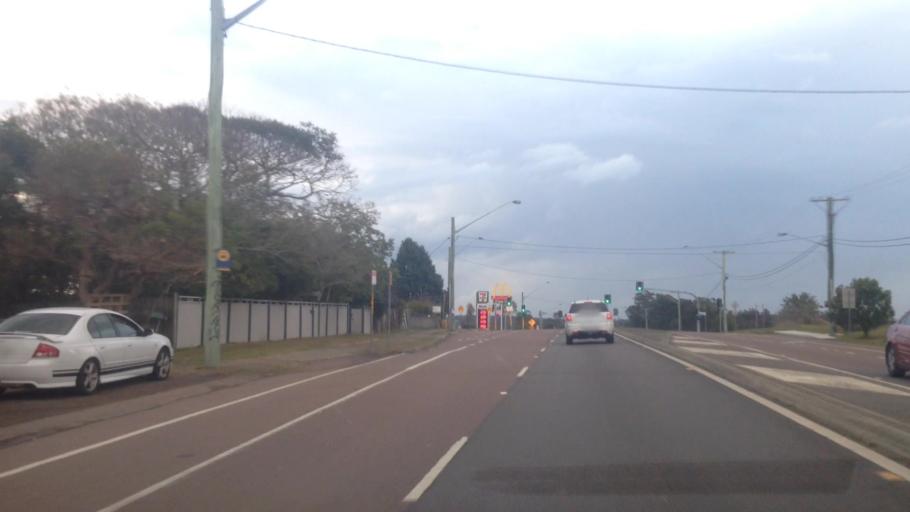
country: AU
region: New South Wales
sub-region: Wyong Shire
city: Tuggerawong
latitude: -33.2665
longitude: 151.4548
